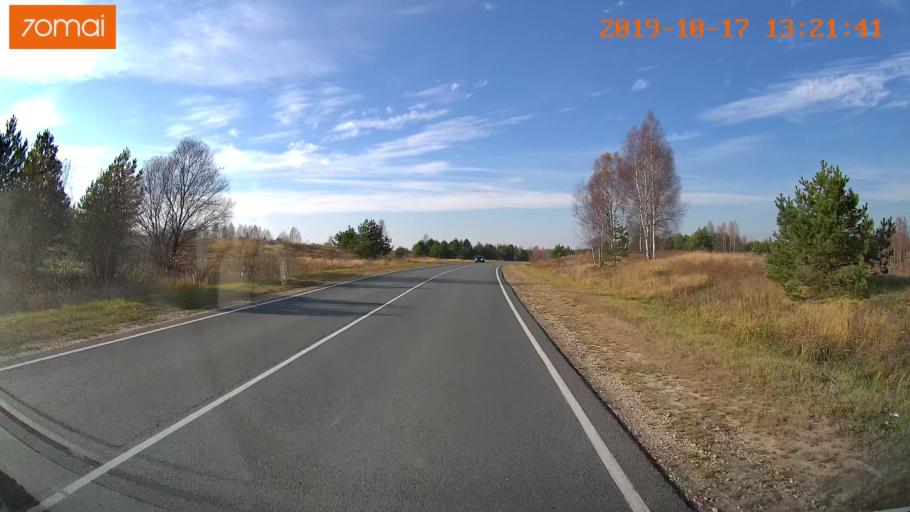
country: RU
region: Rjazan
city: Gus'-Zheleznyy
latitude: 55.0820
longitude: 41.0210
